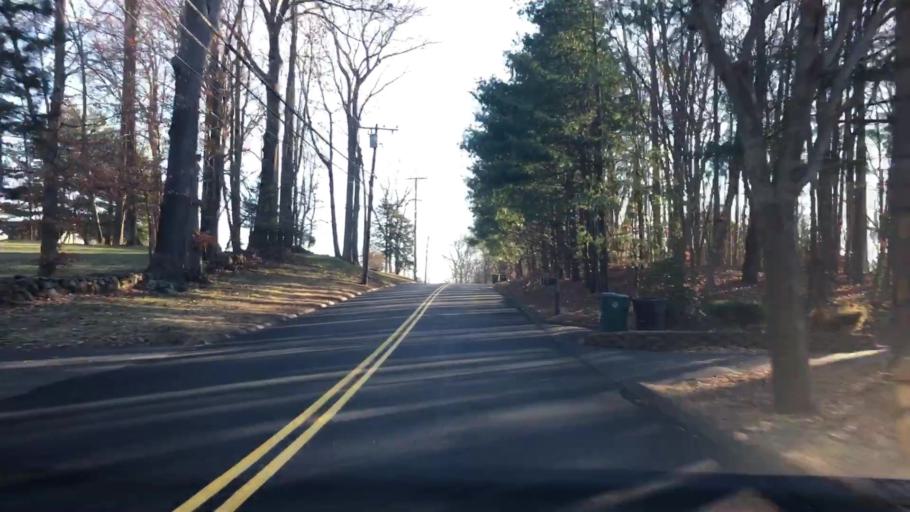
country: US
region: Connecticut
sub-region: New Haven County
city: Meriden
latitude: 41.5479
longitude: -72.8611
